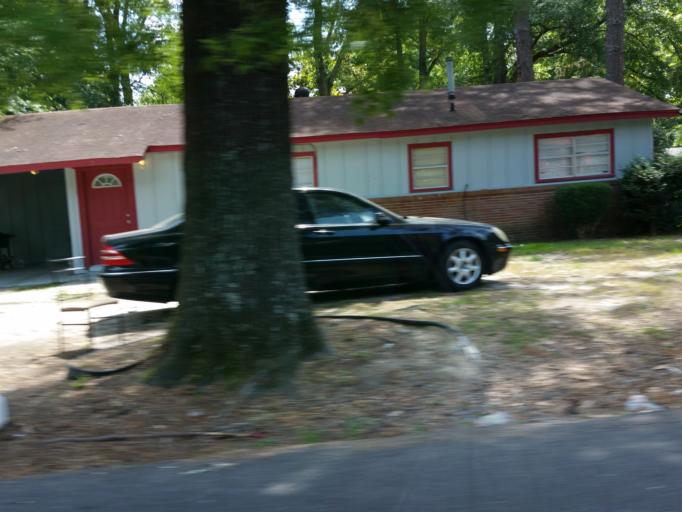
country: US
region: Mississippi
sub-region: Lauderdale County
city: Meridian
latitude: 32.3847
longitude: -88.7203
